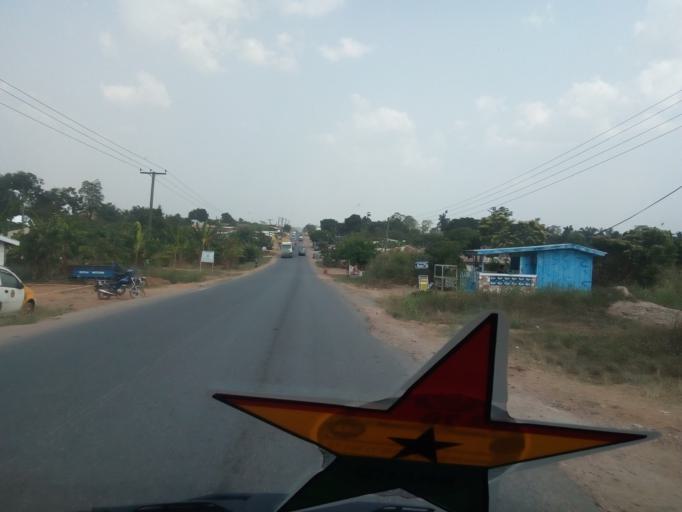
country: GH
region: Eastern
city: Suhum
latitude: 6.0420
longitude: -0.4384
